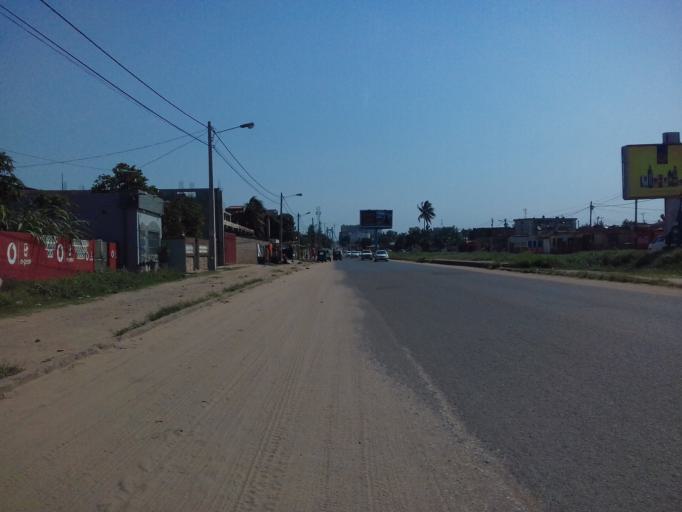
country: MZ
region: Maputo City
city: Maputo
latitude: -25.9464
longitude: 32.5717
